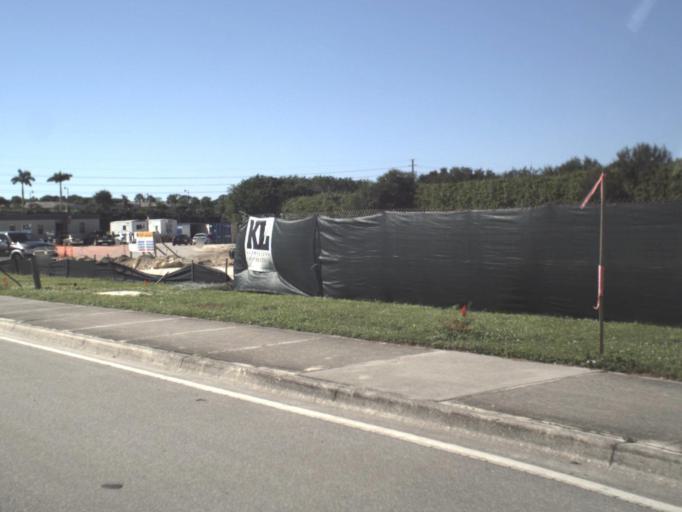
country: US
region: Florida
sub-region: Collier County
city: Naples
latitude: 26.1768
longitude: -81.7673
